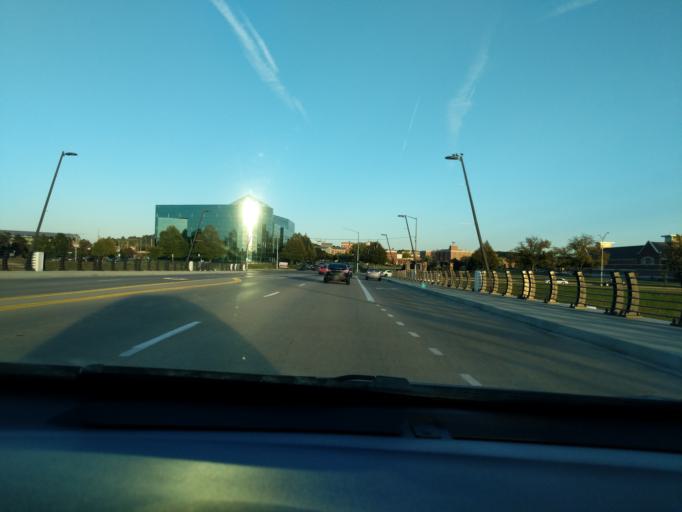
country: US
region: Ohio
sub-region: Montgomery County
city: Dayton
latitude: 39.7400
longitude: -84.1935
